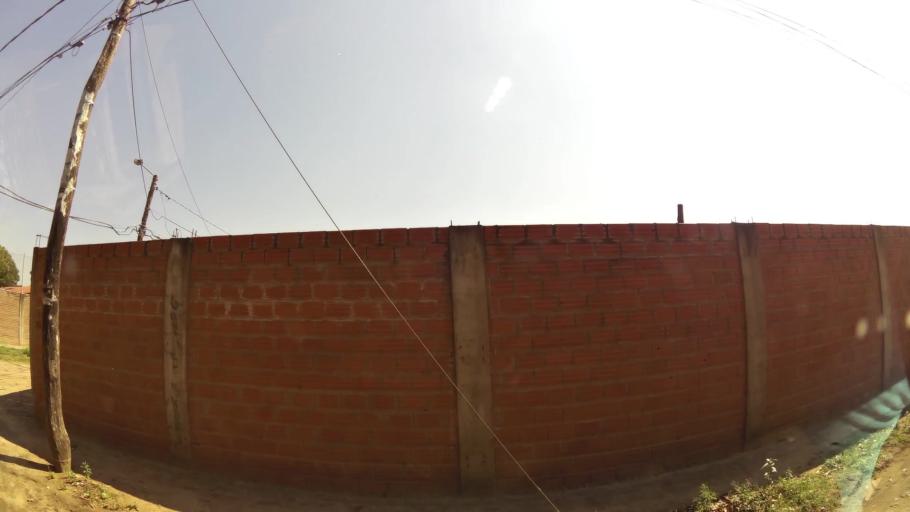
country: BO
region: Santa Cruz
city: Santa Cruz de la Sierra
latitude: -17.7308
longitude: -63.1606
